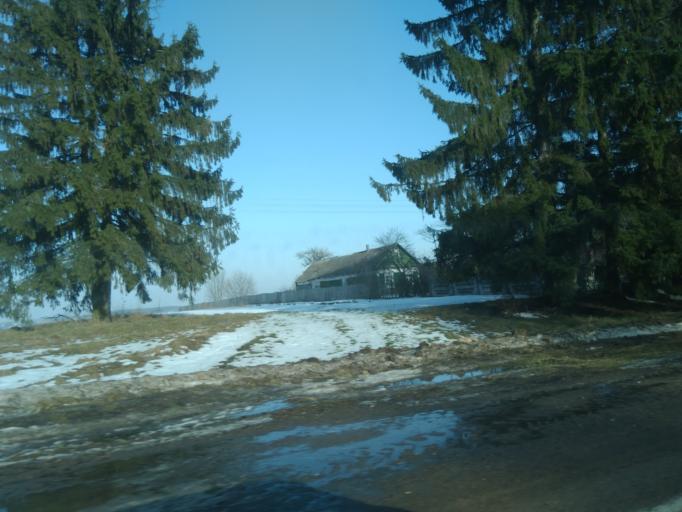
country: BY
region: Minsk
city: Snow
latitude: 53.2134
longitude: 26.4532
